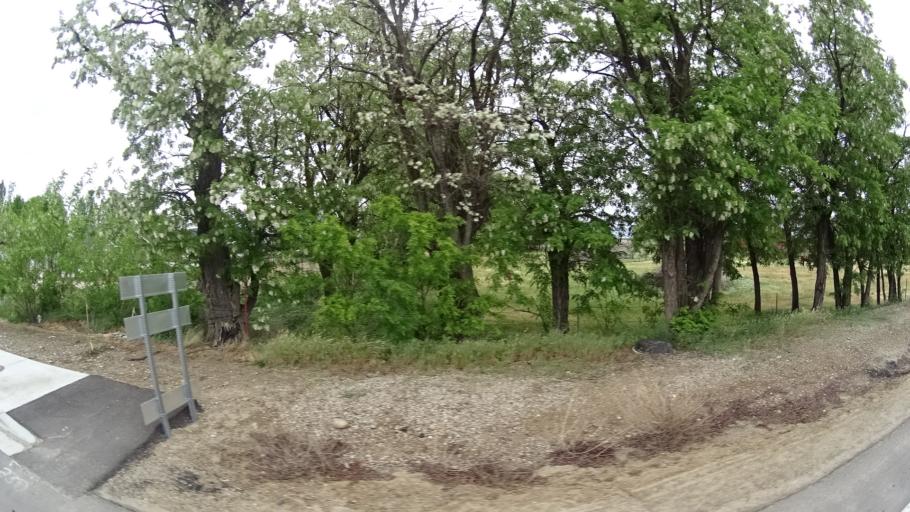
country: US
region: Idaho
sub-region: Ada County
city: Star
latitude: 43.7150
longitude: -116.5031
